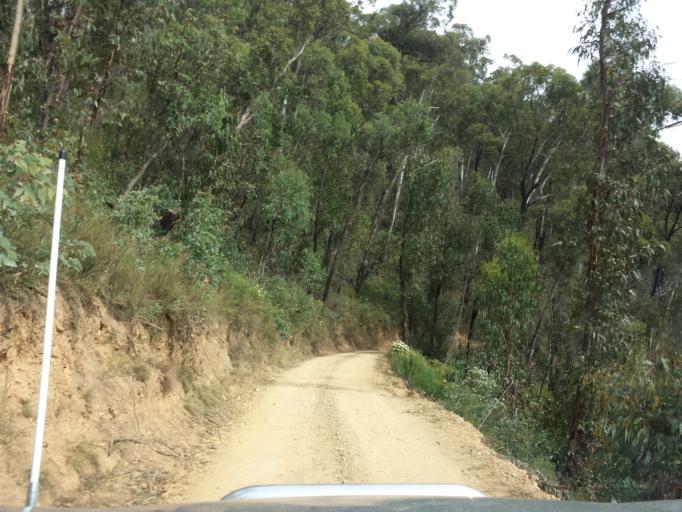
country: AU
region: Victoria
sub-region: Latrobe
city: Moe
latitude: -37.7727
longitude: 146.3884
